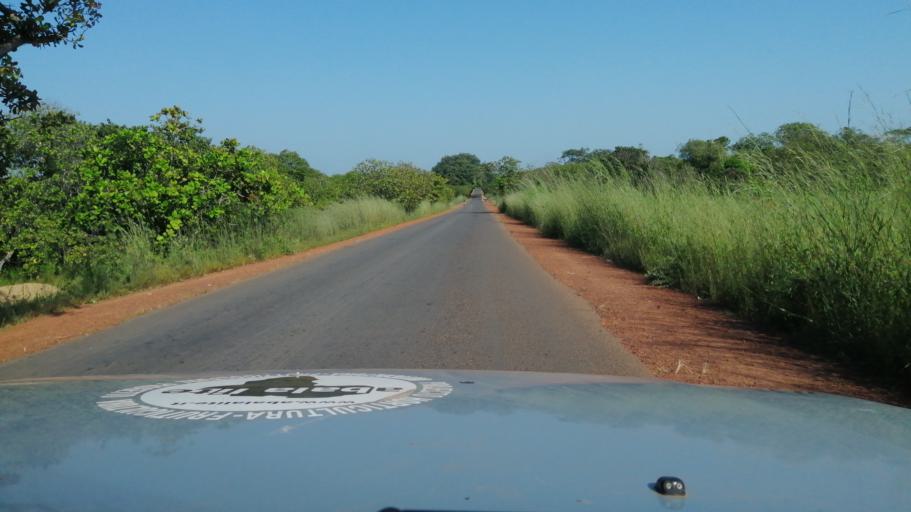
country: GW
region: Bissau
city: Bissau
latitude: 11.9589
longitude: -15.5325
